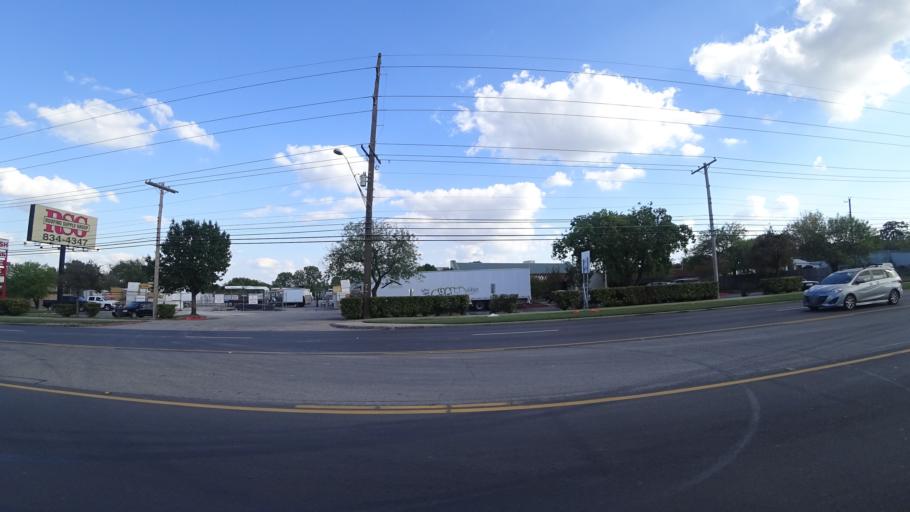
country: US
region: Texas
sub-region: Travis County
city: Austin
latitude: 30.3527
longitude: -97.7067
